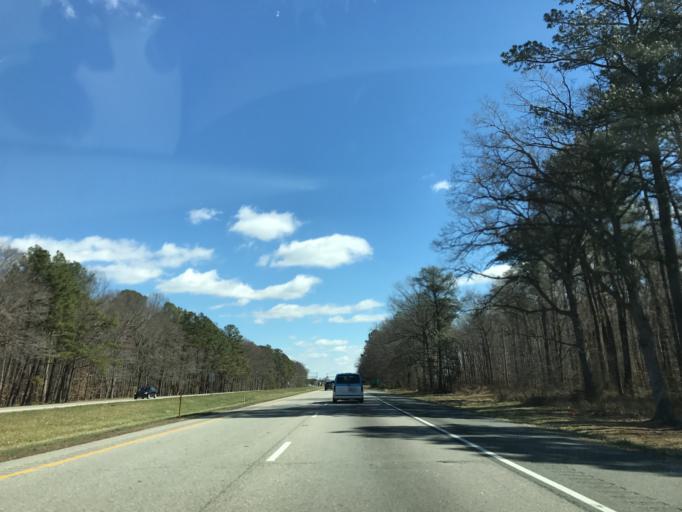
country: US
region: Maryland
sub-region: Queen Anne's County
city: Centreville
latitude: 39.0138
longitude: -76.0886
